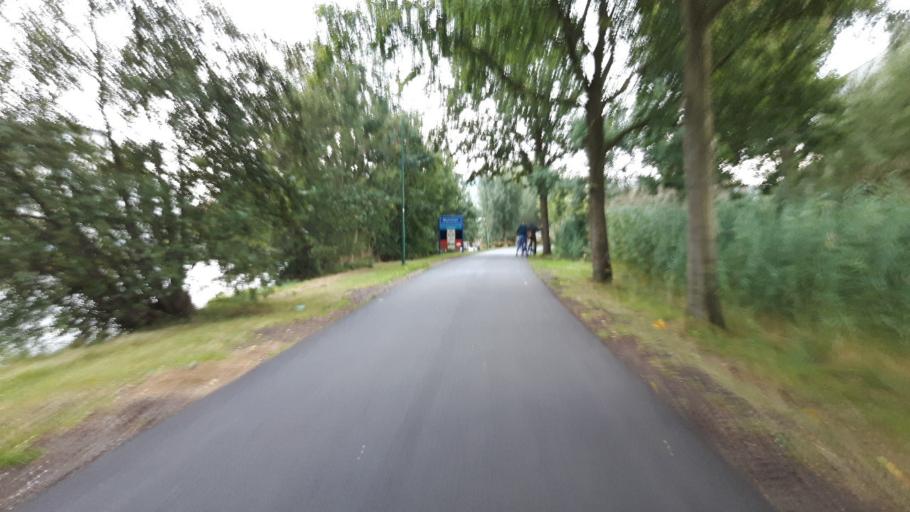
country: NL
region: Utrecht
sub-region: Stichtse Vecht
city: Maarssen
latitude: 52.1297
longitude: 5.0581
